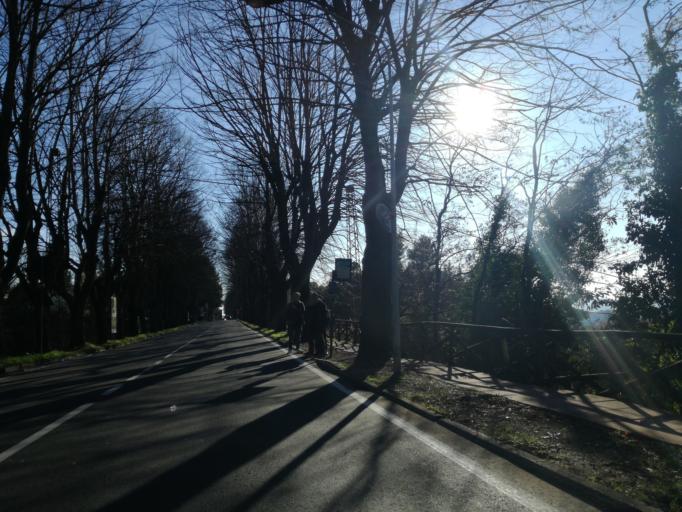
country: IT
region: Umbria
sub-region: Provincia di Perugia
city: Perugia
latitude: 43.0946
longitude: 12.3983
